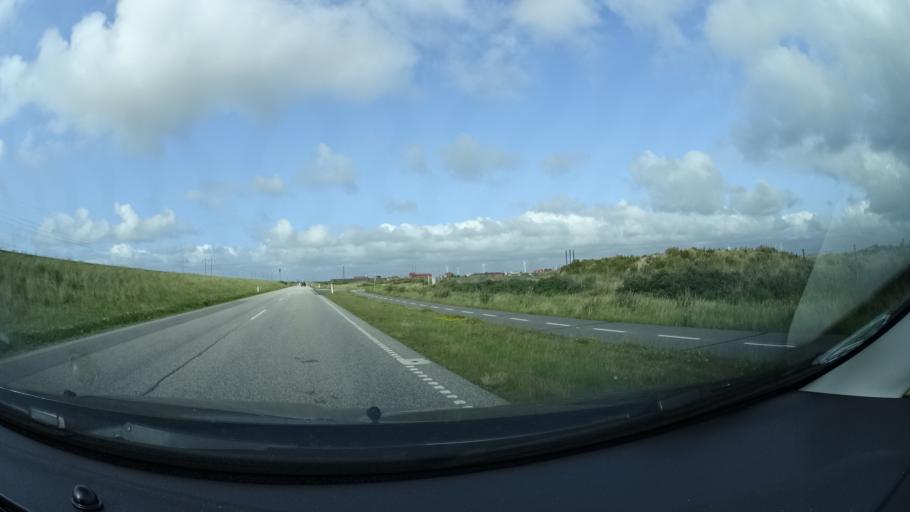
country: DK
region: Central Jutland
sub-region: Lemvig Kommune
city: Harboore
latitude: 56.6499
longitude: 8.1922
